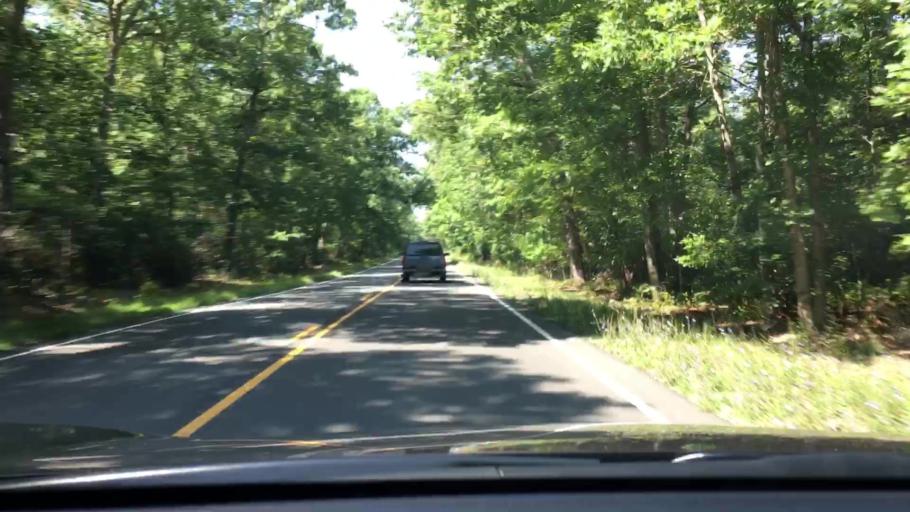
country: US
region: New Jersey
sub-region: Cape May County
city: Woodbine
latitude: 39.2602
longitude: -74.9026
